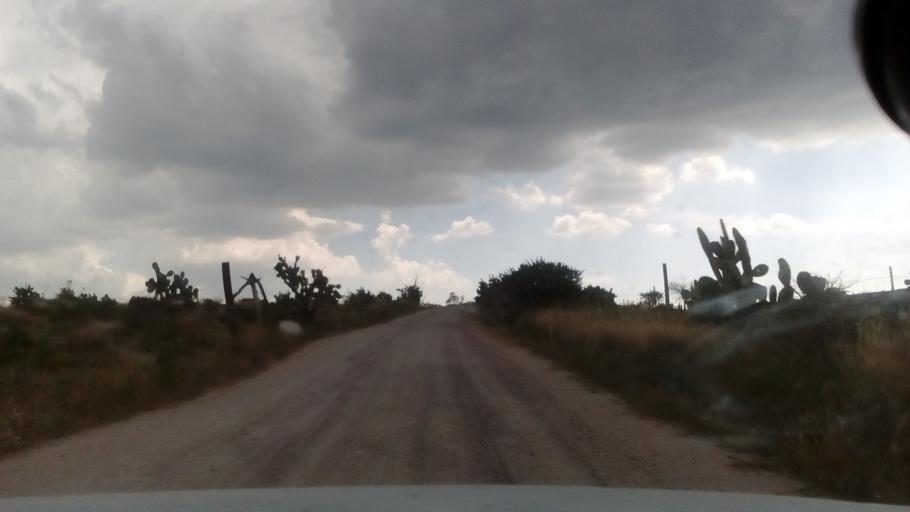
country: MX
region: Guanajuato
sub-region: Silao de la Victoria
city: San Francisco (Banos de Agua Caliente)
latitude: 21.1941
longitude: -101.4228
